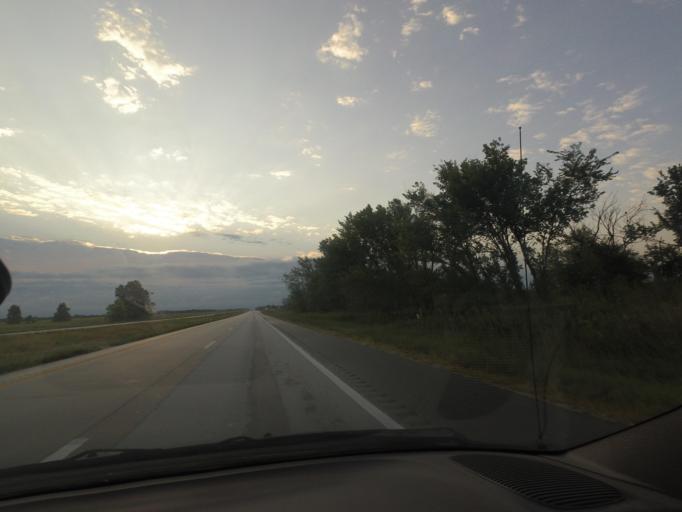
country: US
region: Missouri
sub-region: Shelby County
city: Shelbina
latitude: 39.7282
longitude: -92.1880
